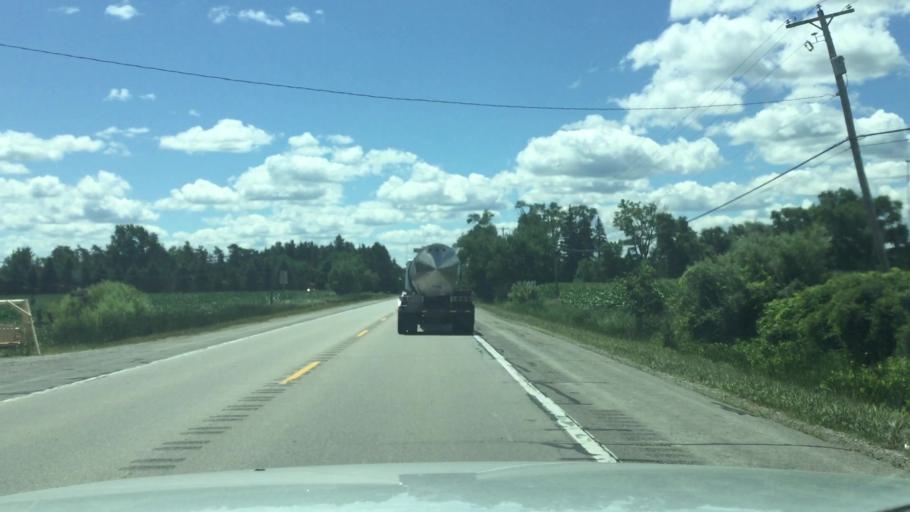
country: US
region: Michigan
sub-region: Saginaw County
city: Shields
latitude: 43.4123
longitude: -84.1309
